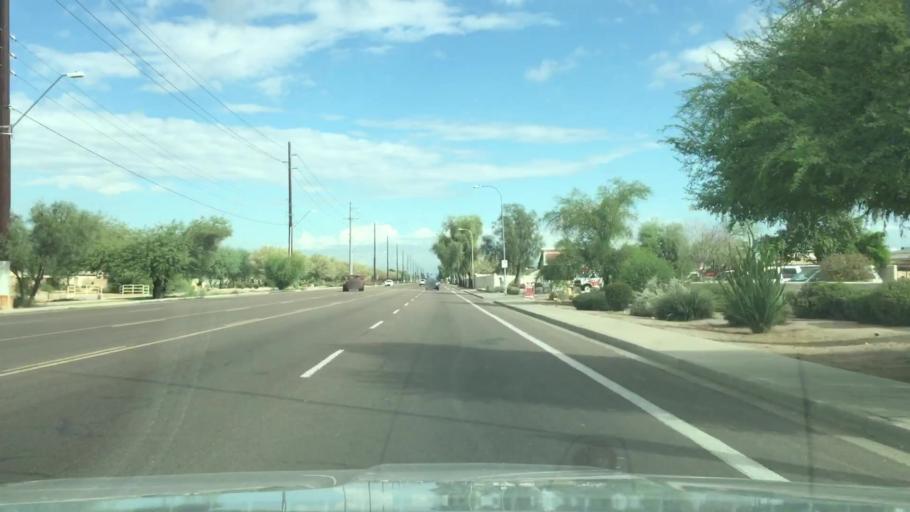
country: US
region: Arizona
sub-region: Maricopa County
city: Tolleson
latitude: 33.4666
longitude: -112.2552
